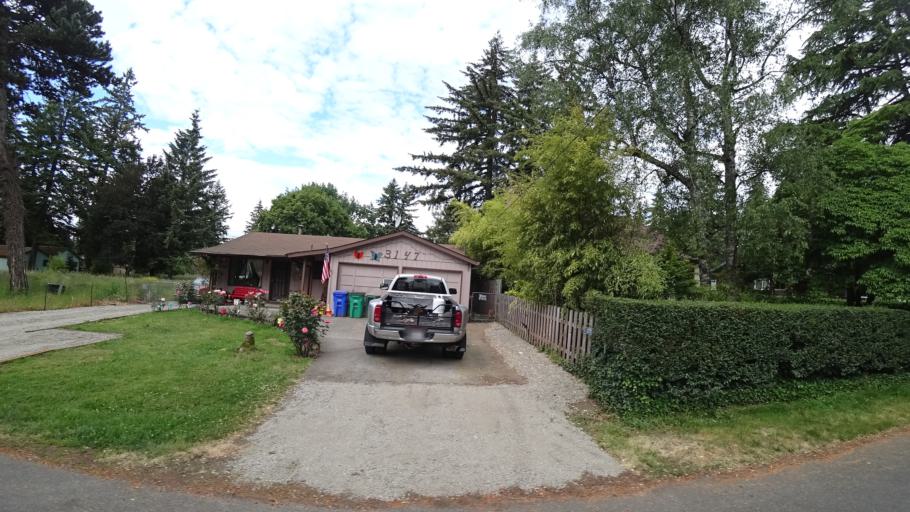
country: US
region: Oregon
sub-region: Multnomah County
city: Lents
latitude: 45.4992
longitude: -122.5312
